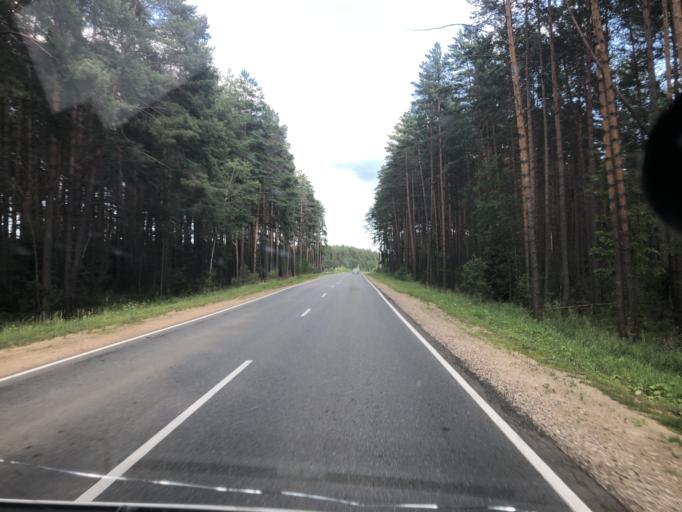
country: RU
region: Kaluga
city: Yukhnov
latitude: 54.7246
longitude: 35.2086
